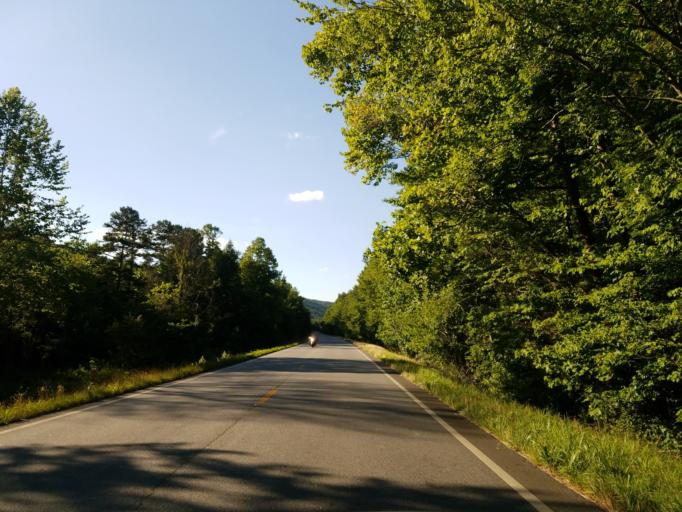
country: US
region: Georgia
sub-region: Whitfield County
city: Dalton
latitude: 34.6303
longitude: -85.0576
